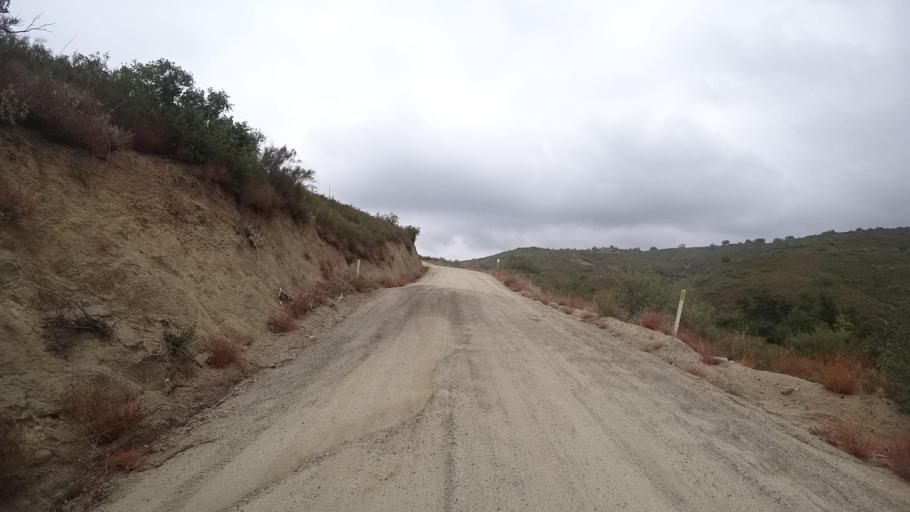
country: US
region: California
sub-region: San Diego County
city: San Diego Country Estates
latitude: 32.9742
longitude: -116.6736
